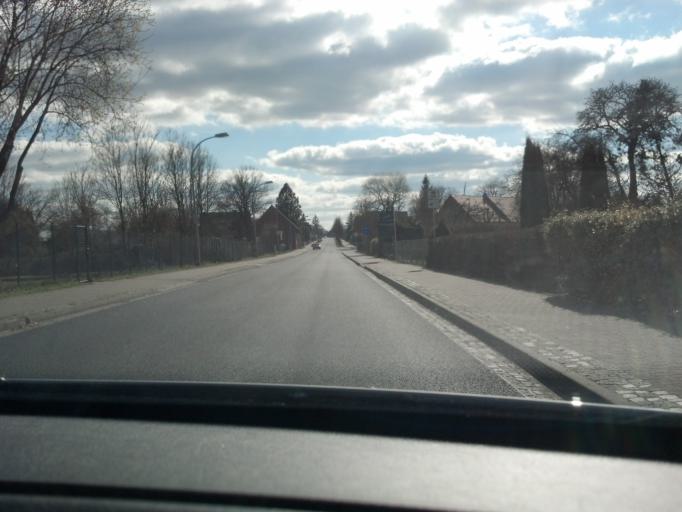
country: DE
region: Brandenburg
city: Gerdshagen
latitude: 53.3101
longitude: 12.2404
